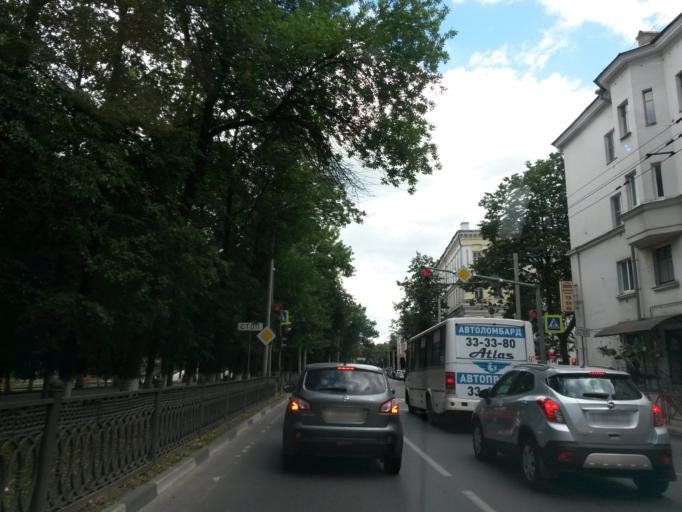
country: RU
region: Jaroslavl
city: Yaroslavl
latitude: 57.6287
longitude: 39.8864
